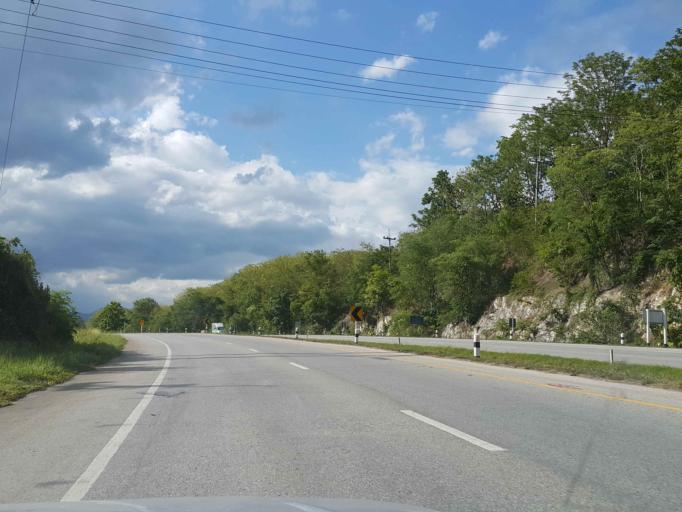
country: TH
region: Lampang
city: Thoen
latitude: 17.6964
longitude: 99.2332
